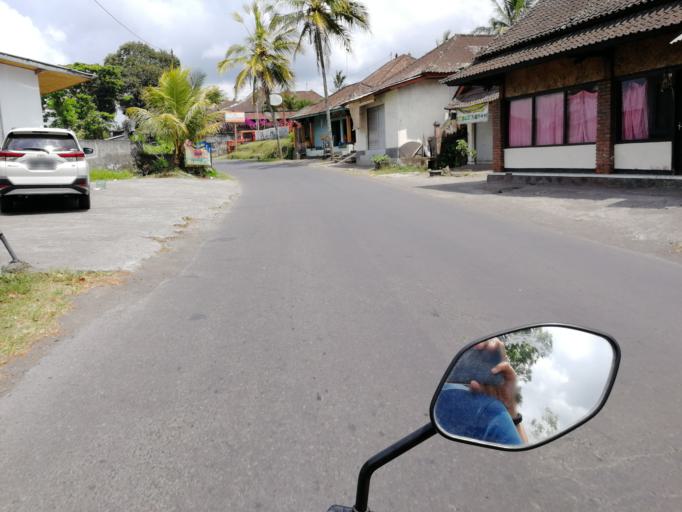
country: ID
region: Bali
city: Banjar Geriana Kangin
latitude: -8.4377
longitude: 115.4791
